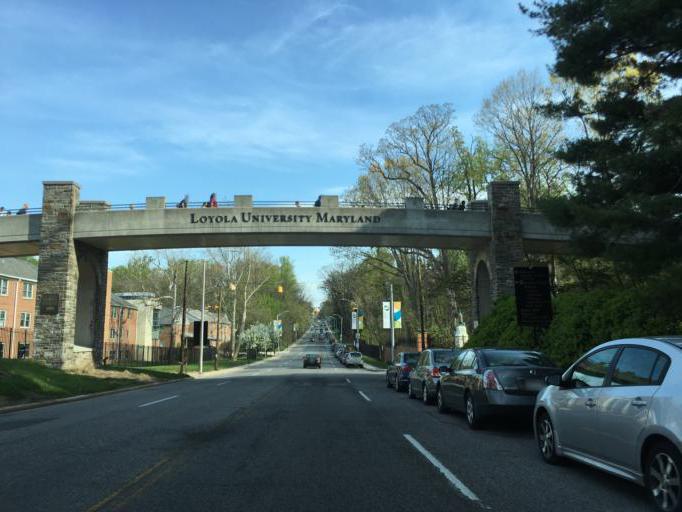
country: US
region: Maryland
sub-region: City of Baltimore
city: Baltimore
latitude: 39.3462
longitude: -76.6222
